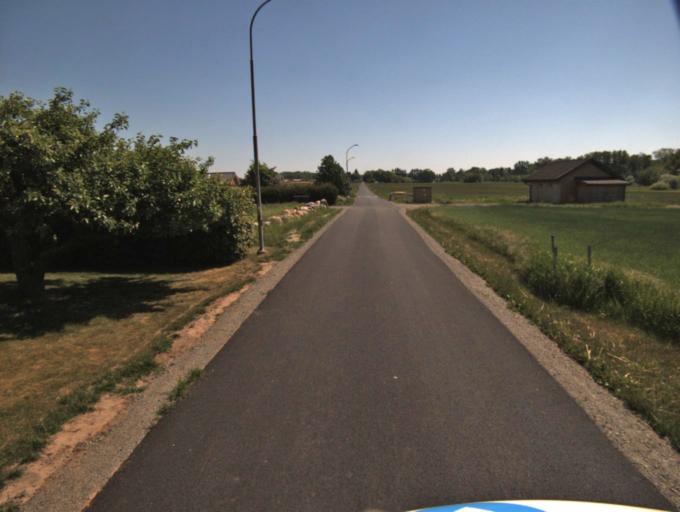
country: SE
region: Skane
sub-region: Kristianstads Kommun
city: Kristianstad
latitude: 56.0173
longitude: 14.2065
